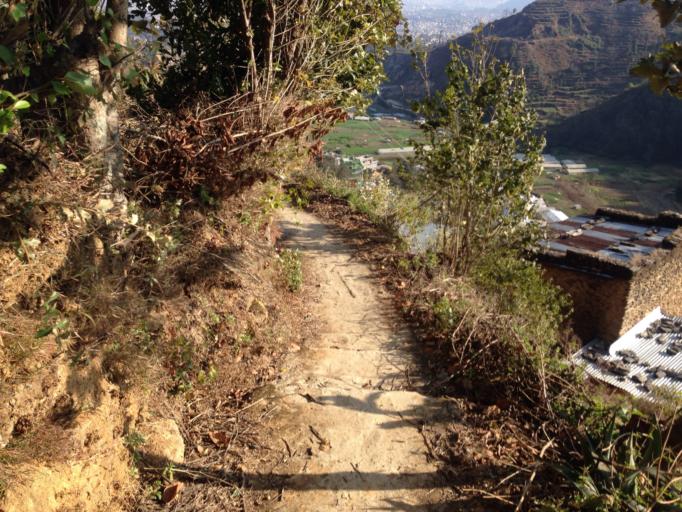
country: NP
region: Central Region
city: Kirtipur
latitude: 27.7315
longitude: 85.2643
